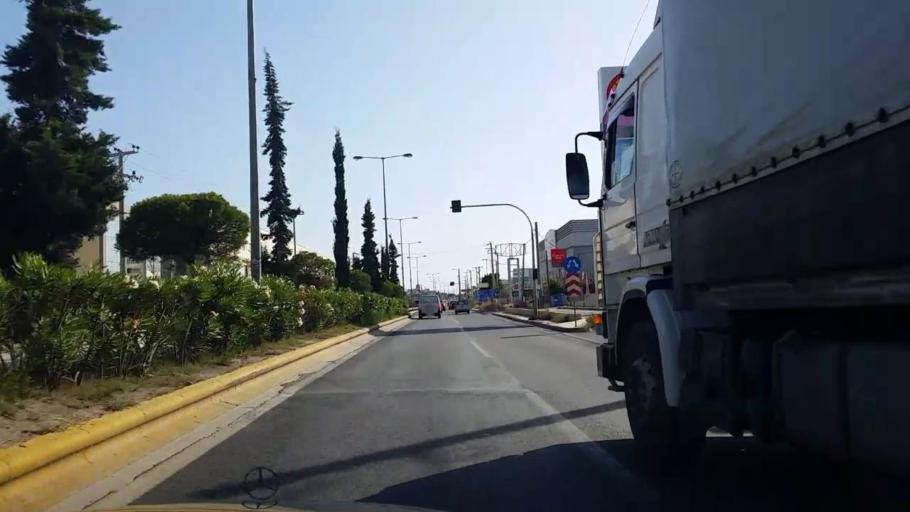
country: GR
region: Attica
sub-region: Nomarchia Anatolikis Attikis
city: Koropi
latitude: 37.8770
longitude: 23.8675
